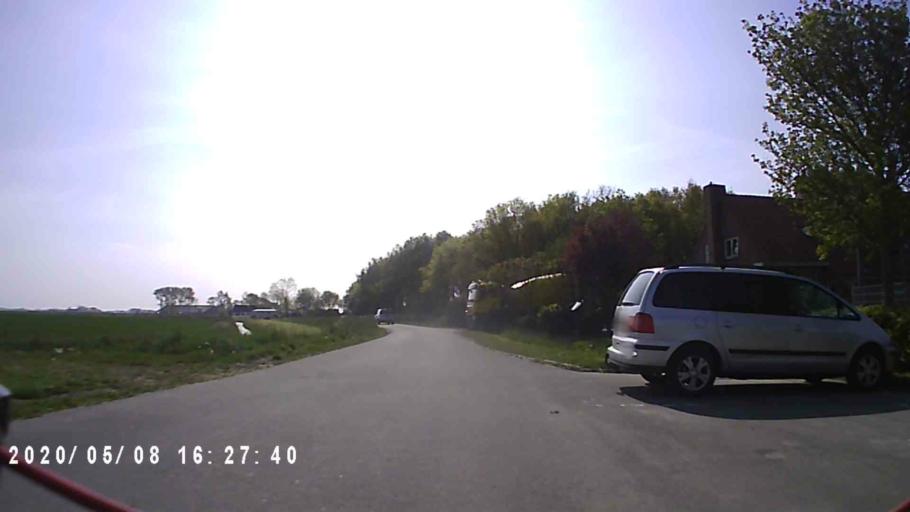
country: NL
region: Groningen
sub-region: Gemeente Bedum
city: Bedum
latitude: 53.3626
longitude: 6.6301
